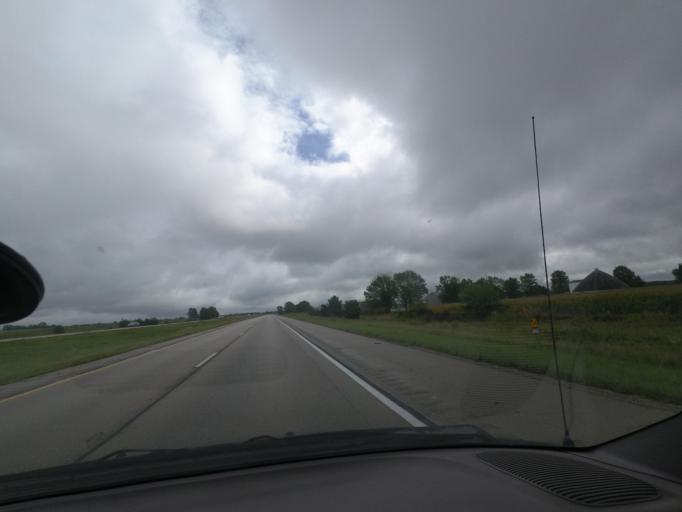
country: US
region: Illinois
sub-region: Piatt County
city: Monticello
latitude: 40.0309
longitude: -88.6184
